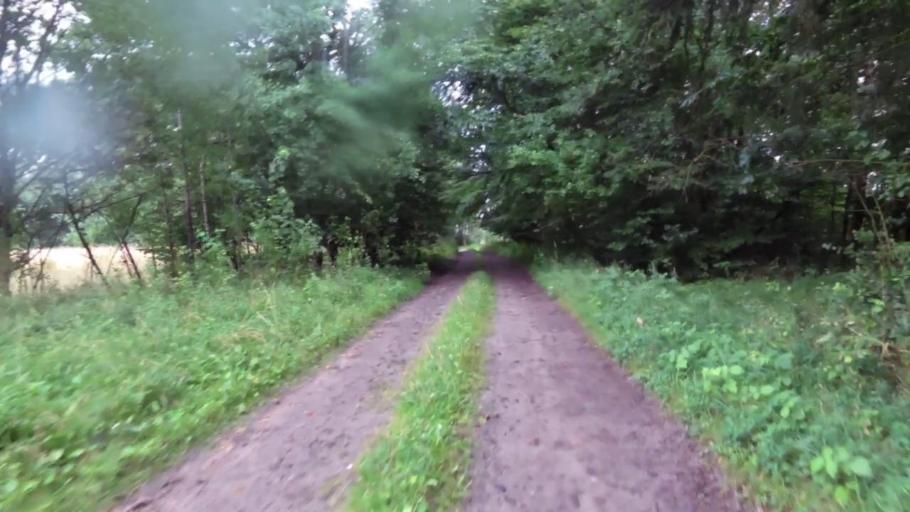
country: PL
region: West Pomeranian Voivodeship
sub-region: Powiat szczecinecki
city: Lubowo
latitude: 53.6133
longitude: 16.3169
